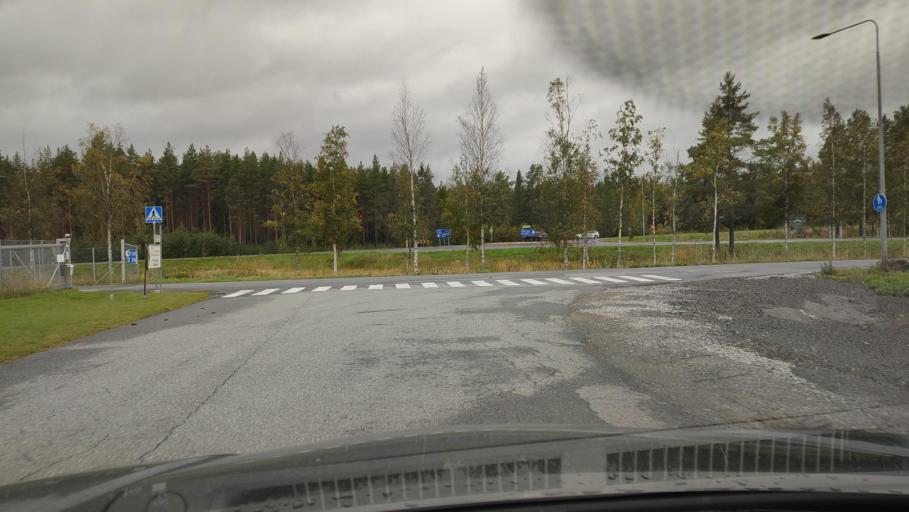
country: FI
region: Ostrobothnia
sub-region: Sydosterbotten
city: Kristinestad
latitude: 62.2278
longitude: 21.5214
